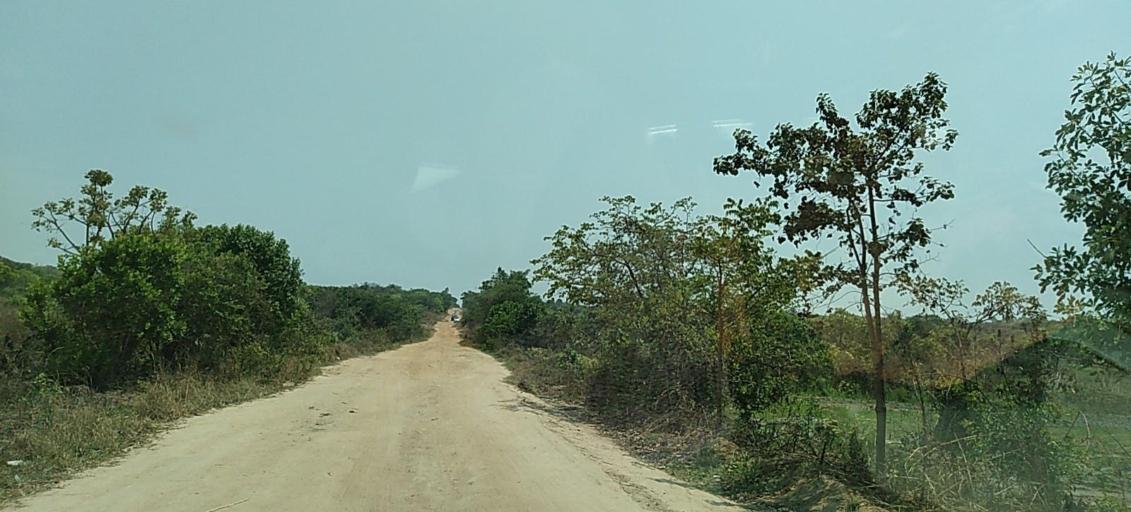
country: ZM
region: Copperbelt
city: Kalulushi
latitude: -12.9330
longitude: 28.1638
